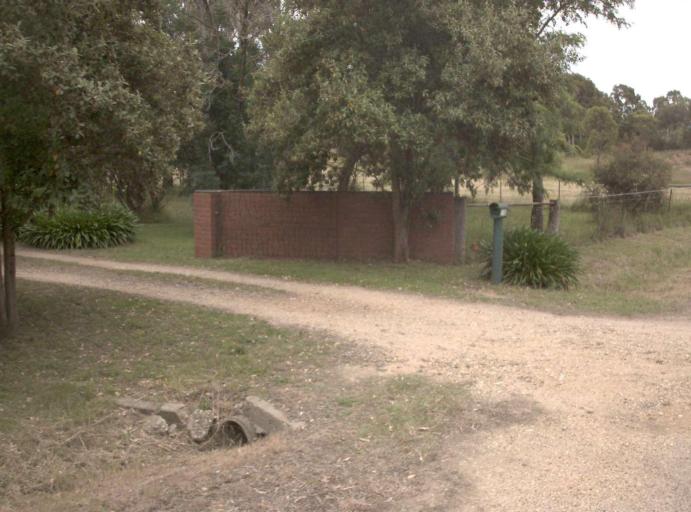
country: AU
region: Victoria
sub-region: East Gippsland
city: Bairnsdale
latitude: -37.8571
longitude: 147.5642
